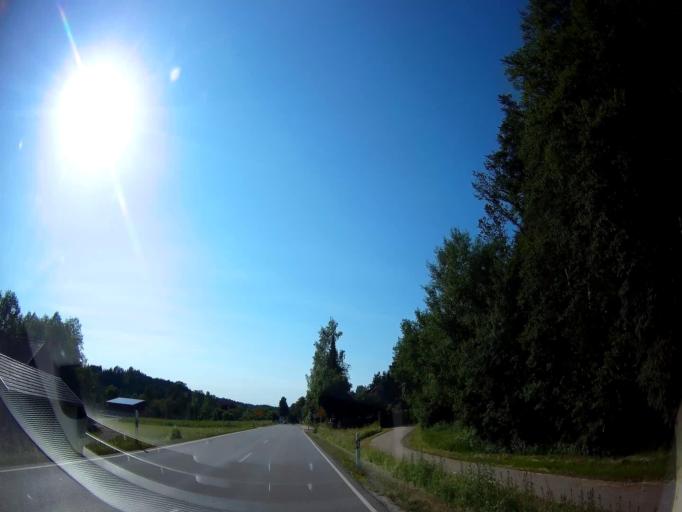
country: DE
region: Bavaria
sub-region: Upper Bavaria
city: Stammham
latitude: 48.2750
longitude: 12.8757
